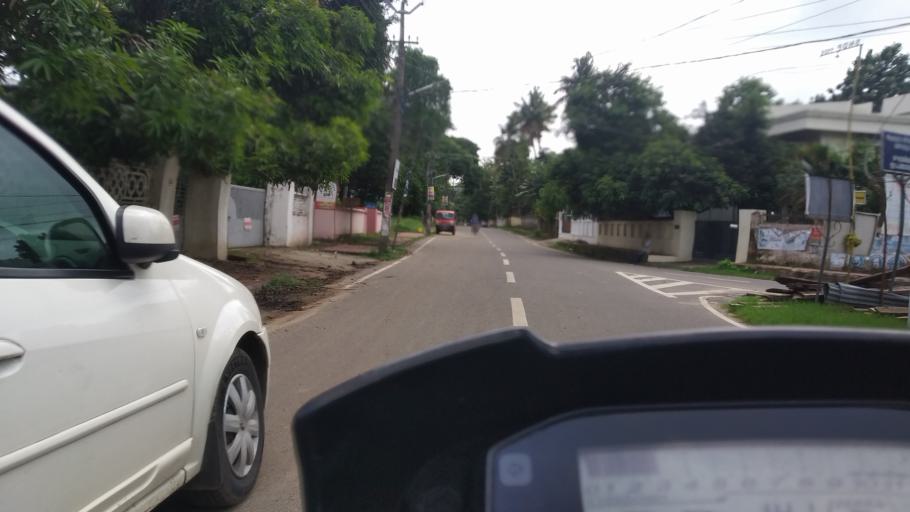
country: IN
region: Kerala
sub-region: Ernakulam
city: Aluva
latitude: 10.1181
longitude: 76.3496
